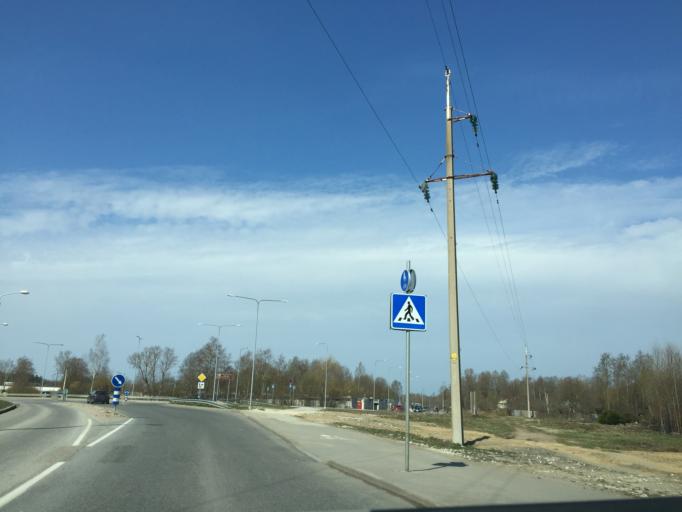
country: EE
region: Ida-Virumaa
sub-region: Narva linn
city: Narva
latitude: 59.3937
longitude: 28.1820
